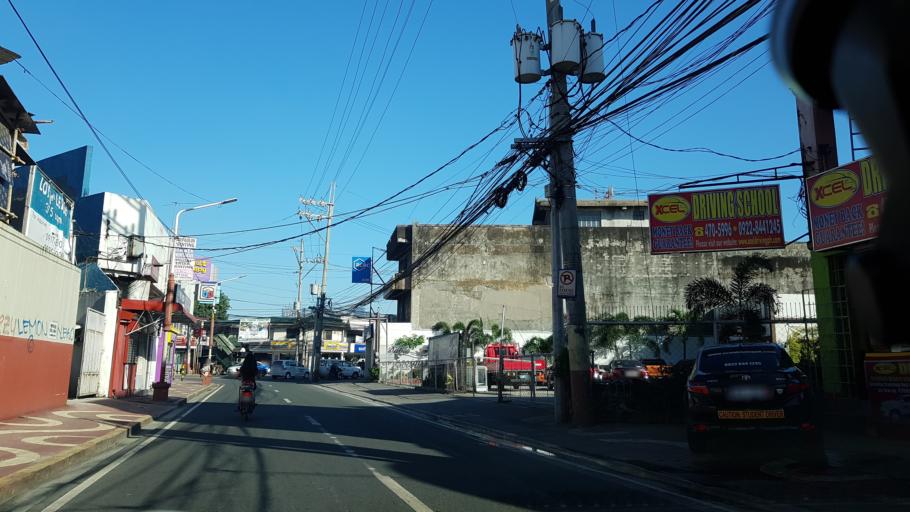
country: PH
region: Calabarzon
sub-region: Province of Rizal
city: Pateros
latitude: 14.5647
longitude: 121.0764
